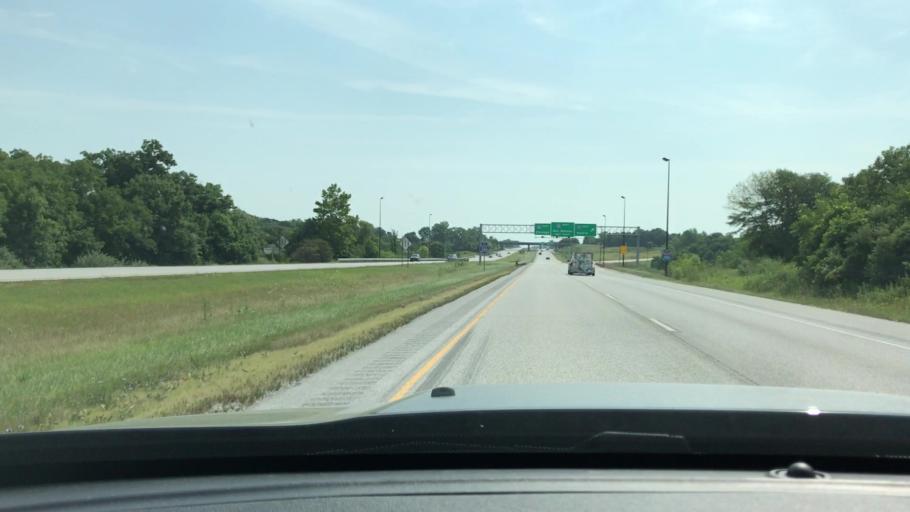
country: US
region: Illinois
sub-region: Henry County
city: Green Rock
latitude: 41.4404
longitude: -90.3402
